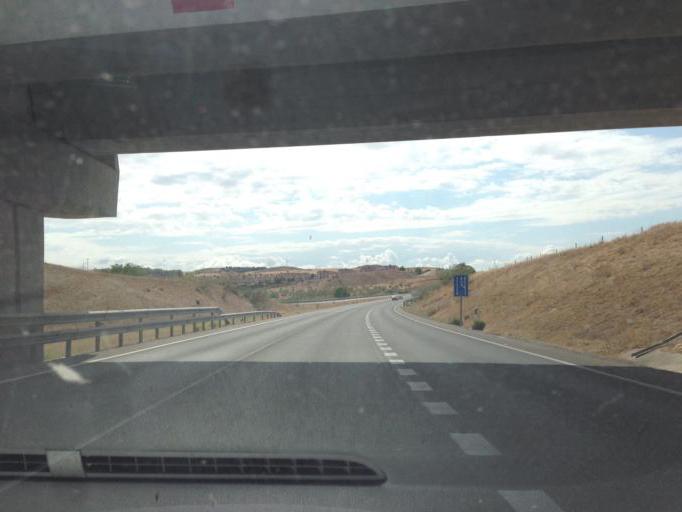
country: ES
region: Madrid
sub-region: Provincia de Madrid
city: Cobena
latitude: 40.5677
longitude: -3.5189
